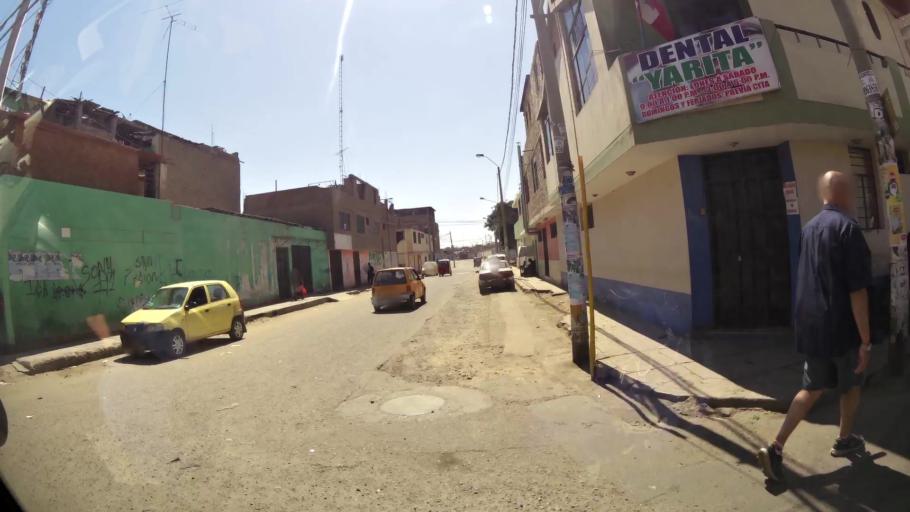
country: PE
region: Ica
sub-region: Provincia de Ica
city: Ica
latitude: -14.0593
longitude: -75.7265
